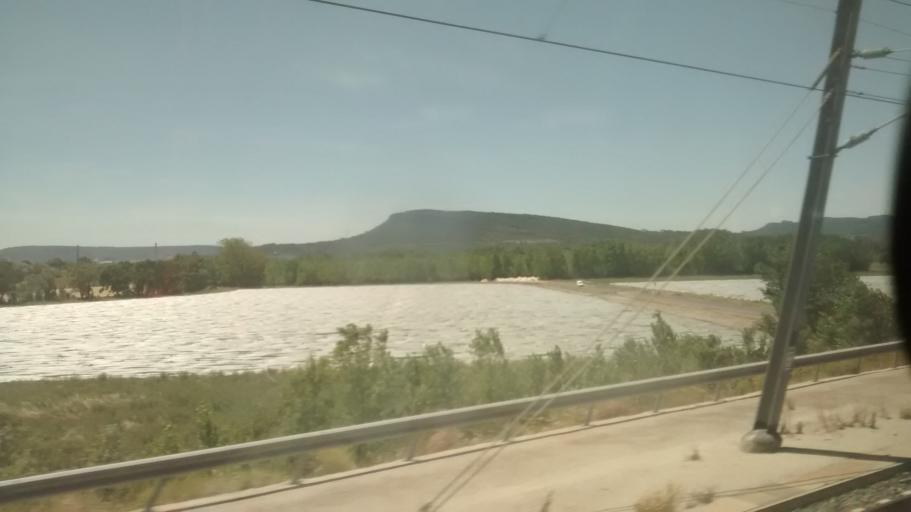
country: FR
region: Provence-Alpes-Cote d'Azur
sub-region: Departement du Vaucluse
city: Piolenc
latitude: 44.1567
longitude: 4.7437
